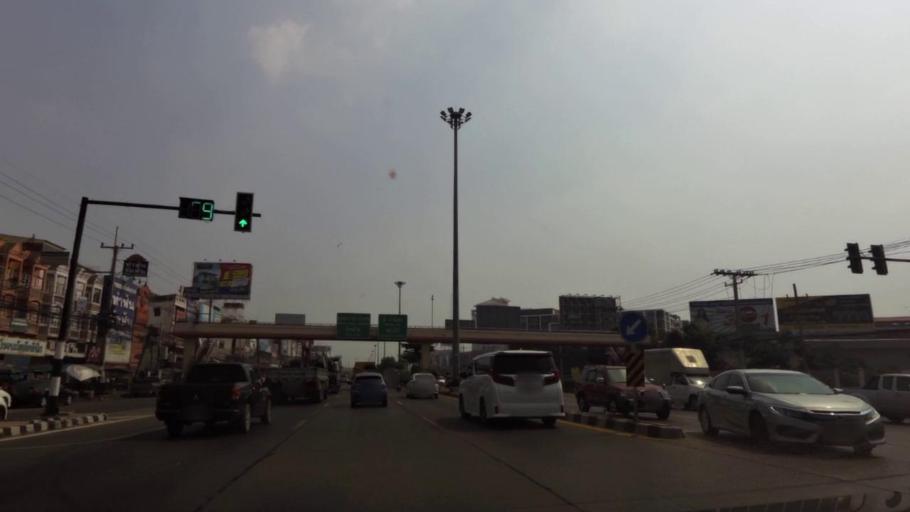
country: TH
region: Phra Nakhon Si Ayutthaya
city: Phra Nakhon Si Ayutthaya
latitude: 14.3485
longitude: 100.6048
